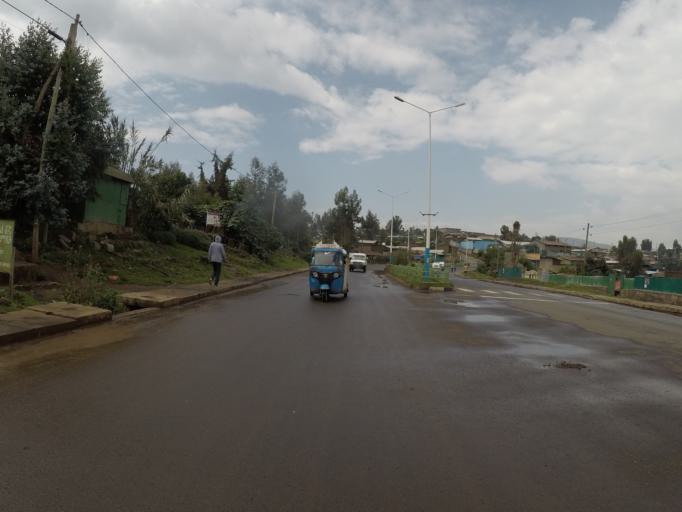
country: ET
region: Amhara
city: Debark'
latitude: 13.1510
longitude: 37.8953
